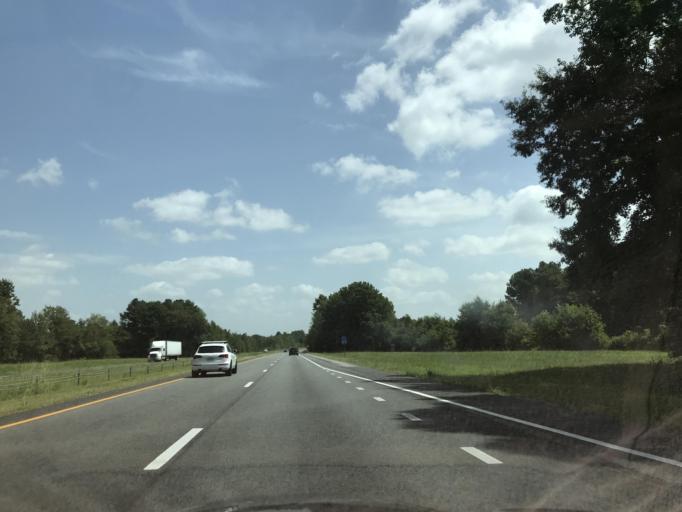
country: US
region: North Carolina
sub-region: Sampson County
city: Plain View
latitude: 35.2242
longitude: -78.3442
